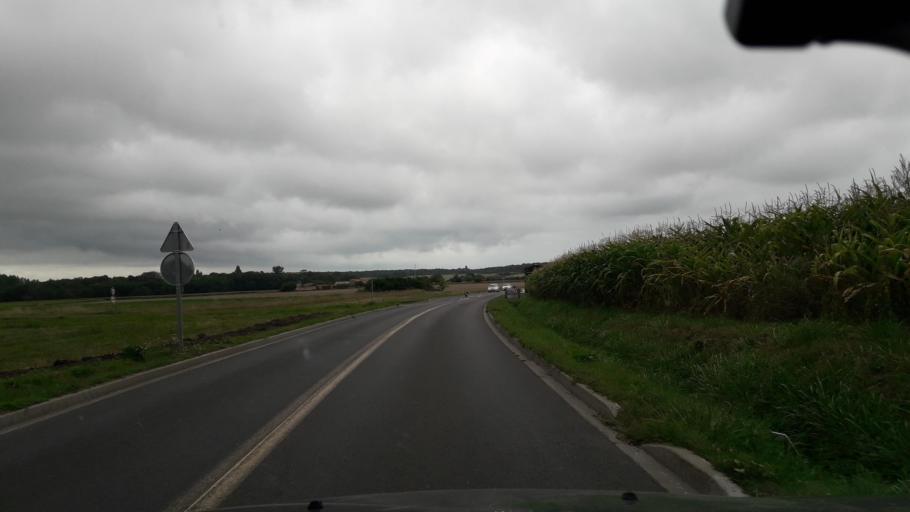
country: FR
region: Poitou-Charentes
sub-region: Departement de la Charente-Maritime
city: Arvert
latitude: 45.7374
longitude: -1.1284
